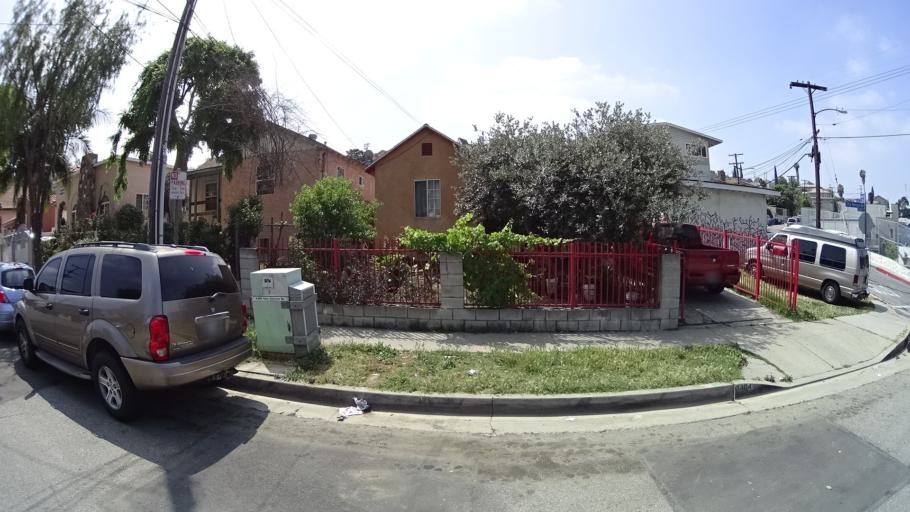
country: US
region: California
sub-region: Los Angeles County
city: Belvedere
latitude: 34.0577
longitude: -118.1704
